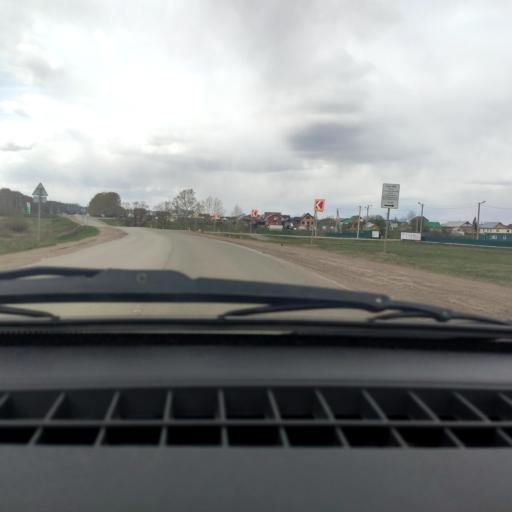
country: RU
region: Bashkortostan
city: Kushnarenkovo
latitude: 55.0791
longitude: 55.3939
